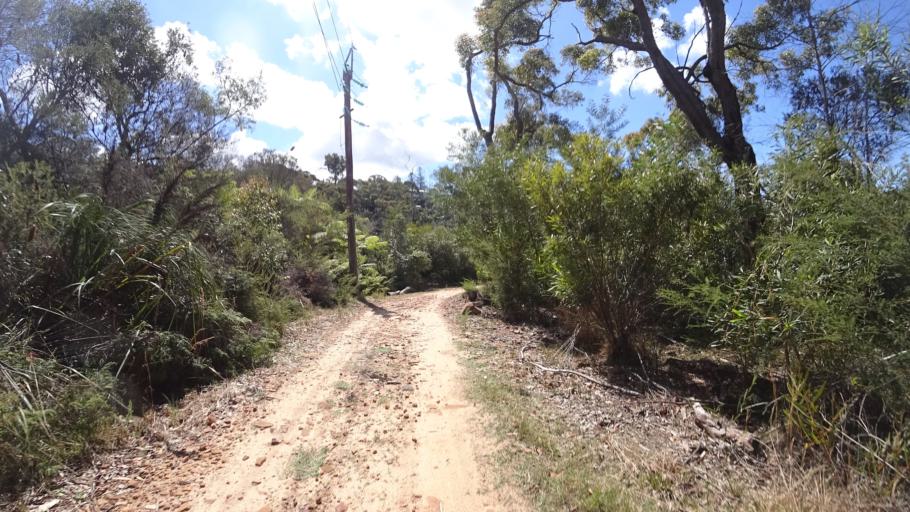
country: AU
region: New South Wales
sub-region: Warringah
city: Killarney Heights
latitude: -33.7627
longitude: 151.2221
